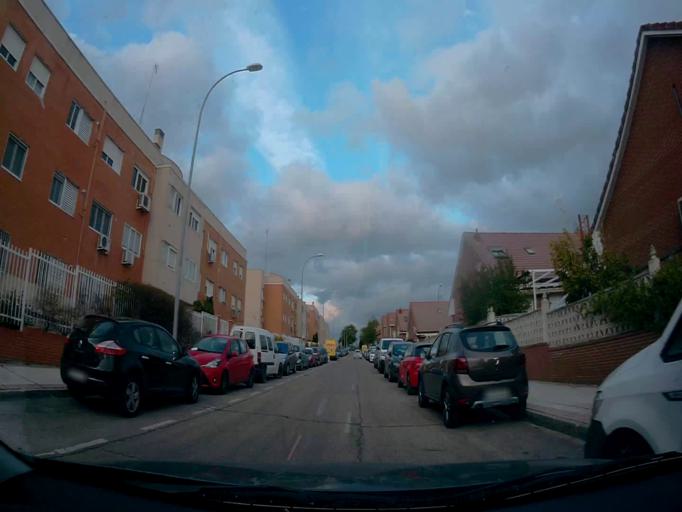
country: ES
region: Madrid
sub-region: Provincia de Madrid
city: Alcorcon
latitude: 40.3364
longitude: -3.8273
